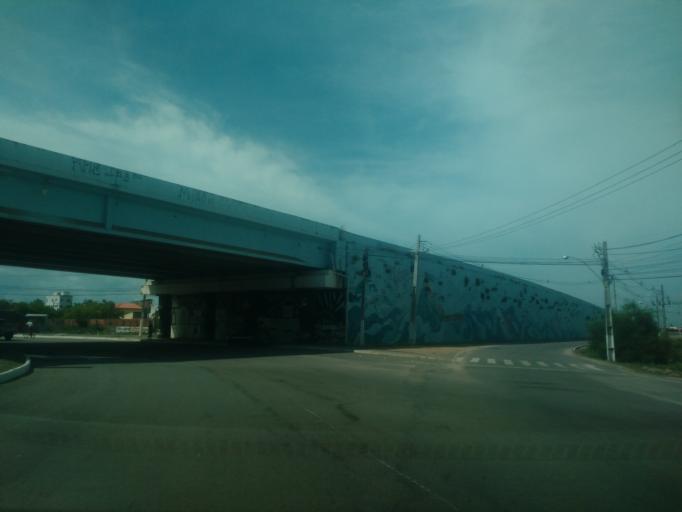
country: BR
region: Alagoas
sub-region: Marechal Deodoro
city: Marechal Deodoro
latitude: -9.7669
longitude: -35.8515
